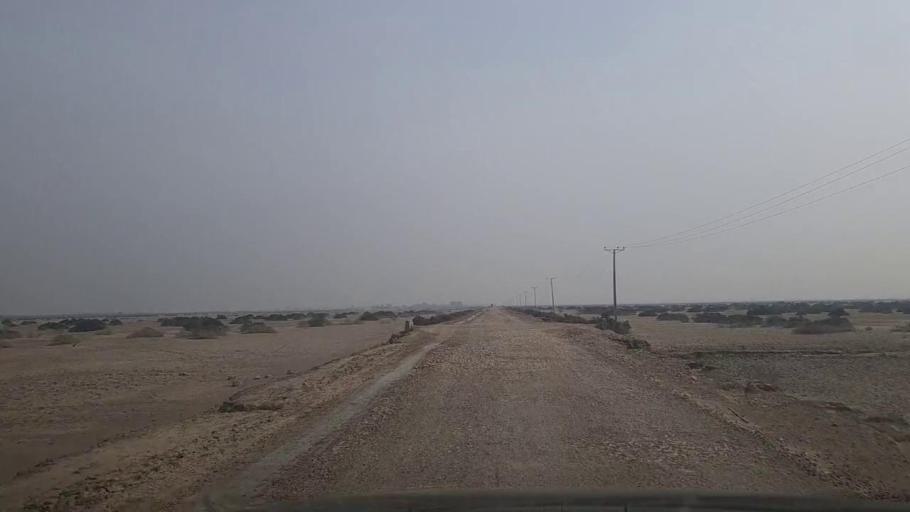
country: PK
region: Sindh
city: Mirpur Sakro
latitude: 24.4667
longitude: 67.6827
